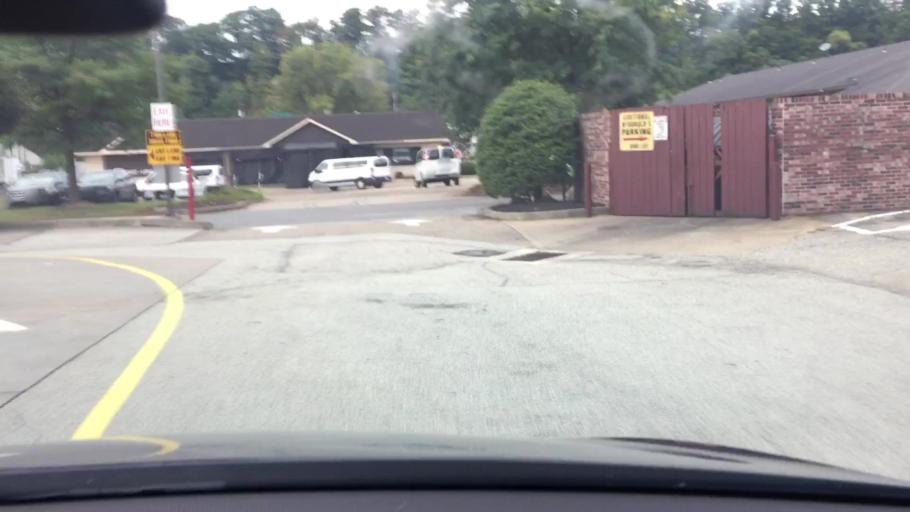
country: US
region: Pennsylvania
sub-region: Allegheny County
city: Oakmont
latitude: 40.5392
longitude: -79.8300
